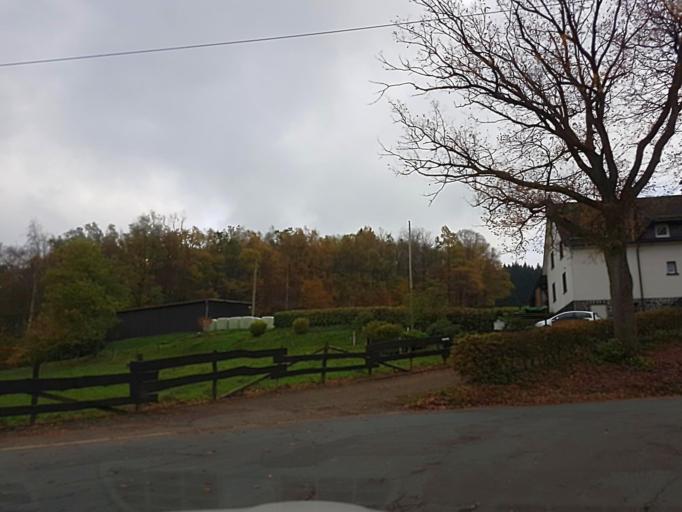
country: DE
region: North Rhine-Westphalia
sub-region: Regierungsbezirk Arnsberg
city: Drolshagen
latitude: 51.0602
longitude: 7.7742
